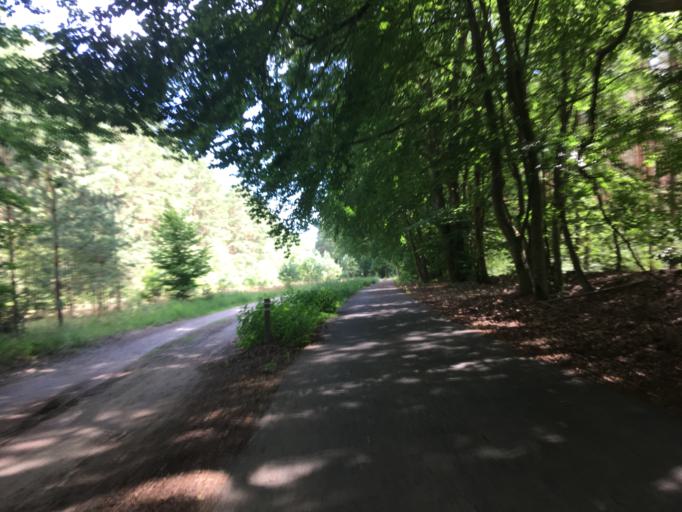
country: DE
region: Brandenburg
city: Rheinsberg
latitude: 53.0746
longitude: 12.9059
